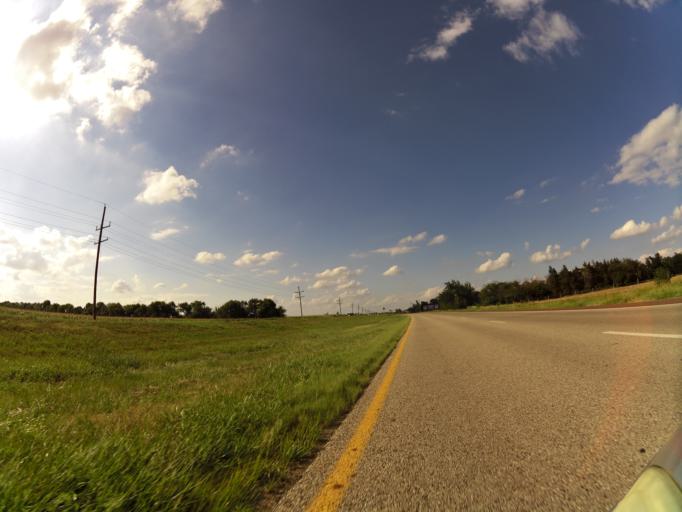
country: US
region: Kansas
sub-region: Reno County
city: South Hutchinson
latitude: 37.9904
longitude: -97.9399
